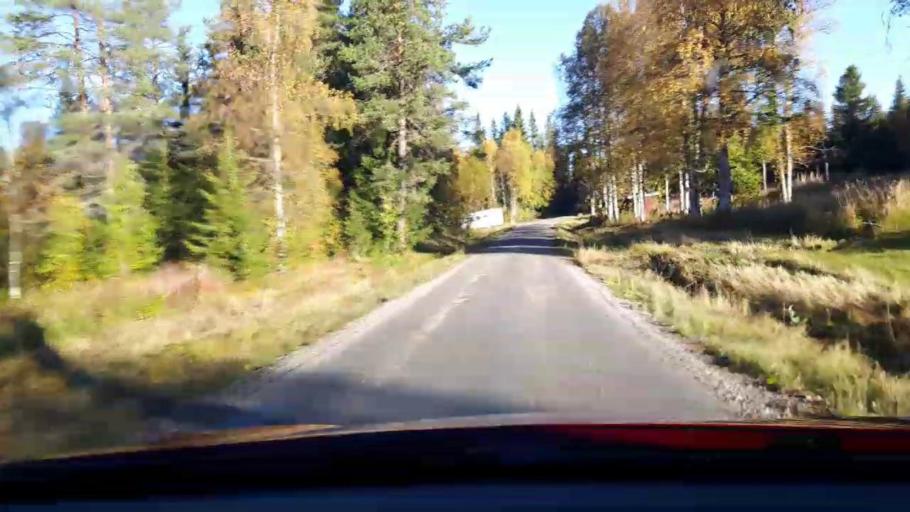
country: SE
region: Jaemtland
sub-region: Stroemsunds Kommun
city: Stroemsund
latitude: 64.3982
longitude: 15.1447
